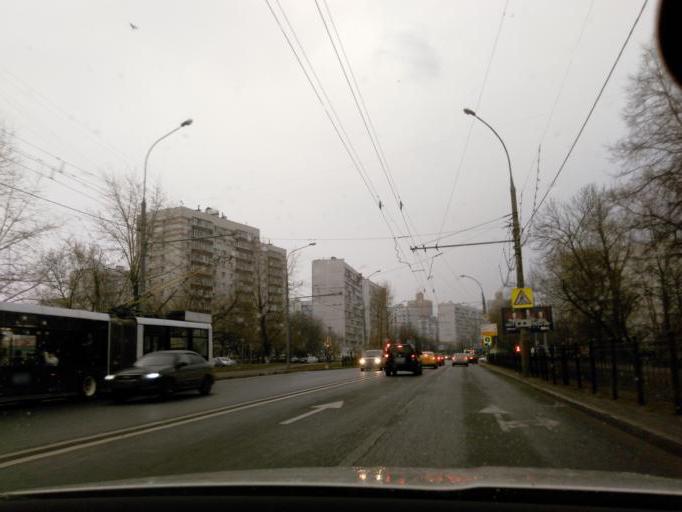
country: RU
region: Moskovskaya
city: Levoberezhnyy
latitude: 55.8455
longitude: 37.4543
